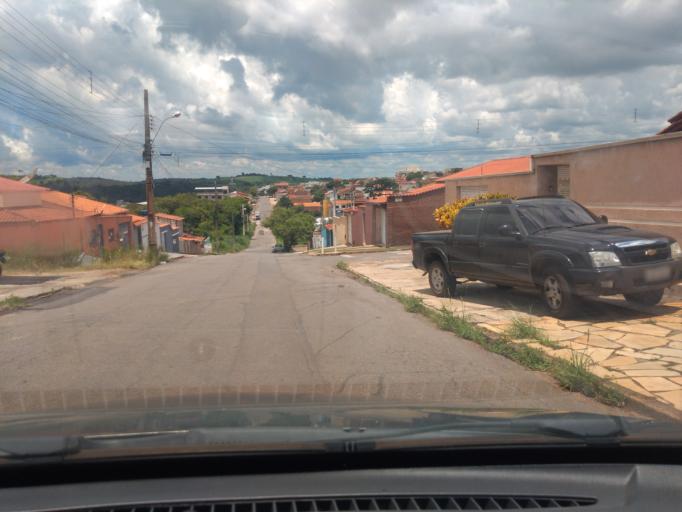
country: BR
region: Minas Gerais
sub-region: Tres Coracoes
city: Tres Coracoes
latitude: -21.6802
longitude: -45.2738
